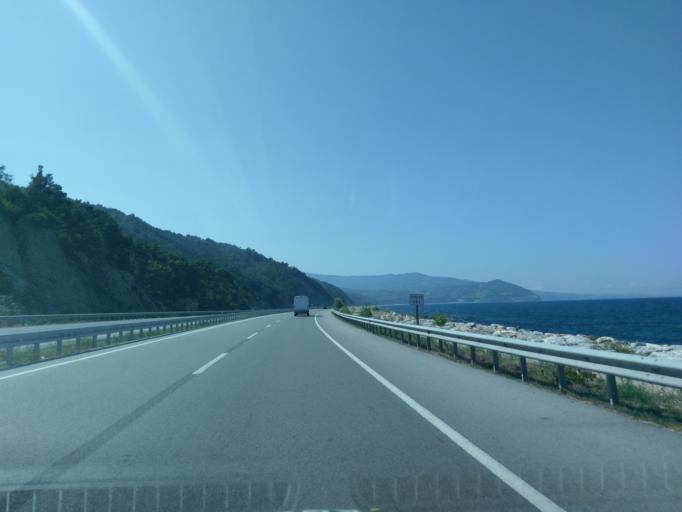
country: TR
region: Sinop
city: Dikmen
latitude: 41.7011
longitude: 35.3338
